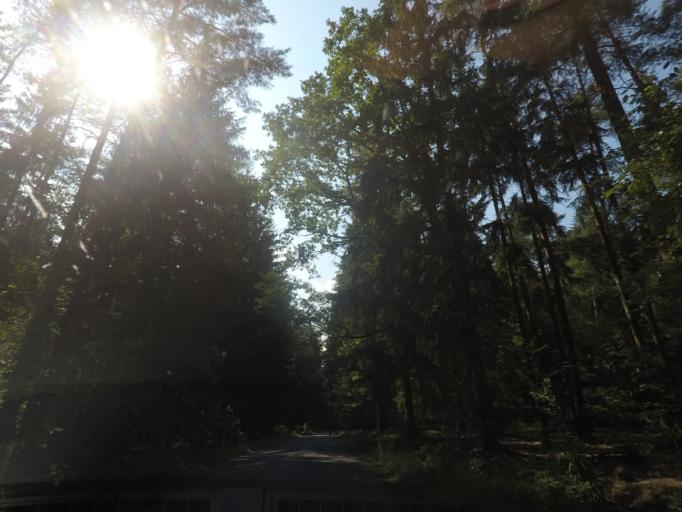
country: CZ
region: Pardubicky
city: Horni Jeleni
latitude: 50.0645
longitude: 16.0745
